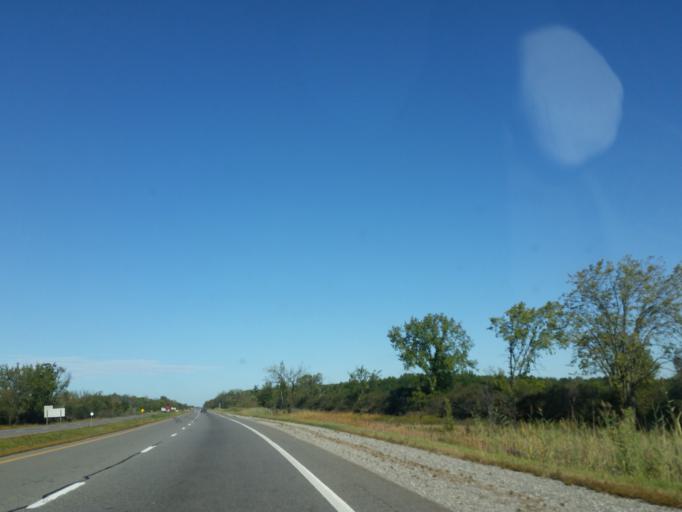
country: US
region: New York
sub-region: Niagara County
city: Niagara Falls
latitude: 43.0012
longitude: -79.0706
